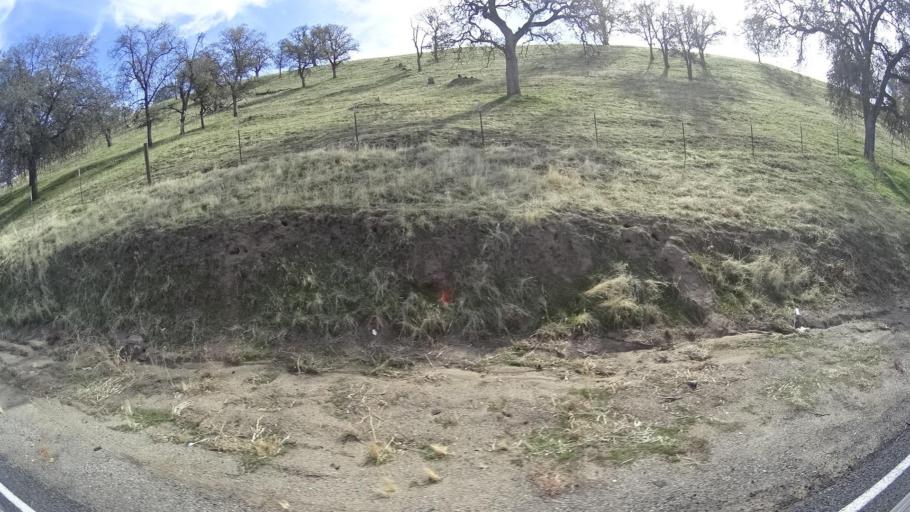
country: US
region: California
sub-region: Kern County
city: Oildale
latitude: 35.6247
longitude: -118.8428
